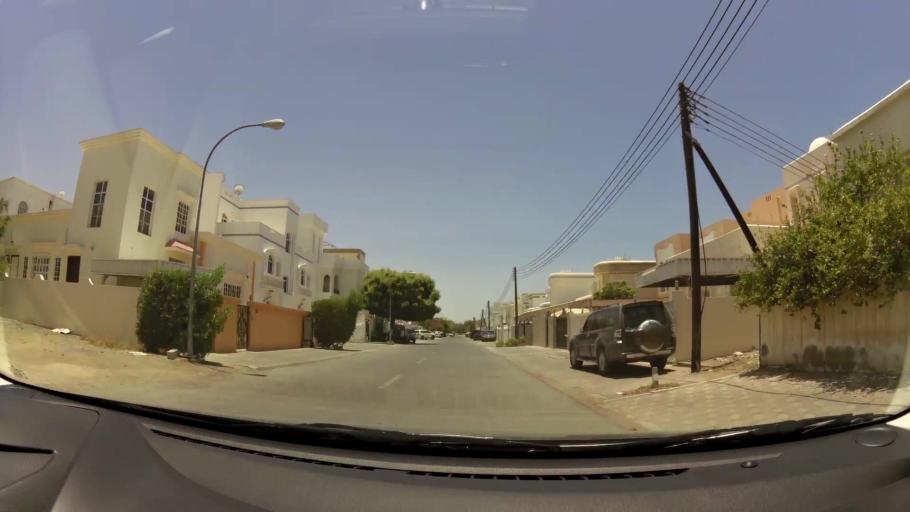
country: OM
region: Muhafazat Masqat
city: Bawshar
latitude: 23.5947
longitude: 58.3937
